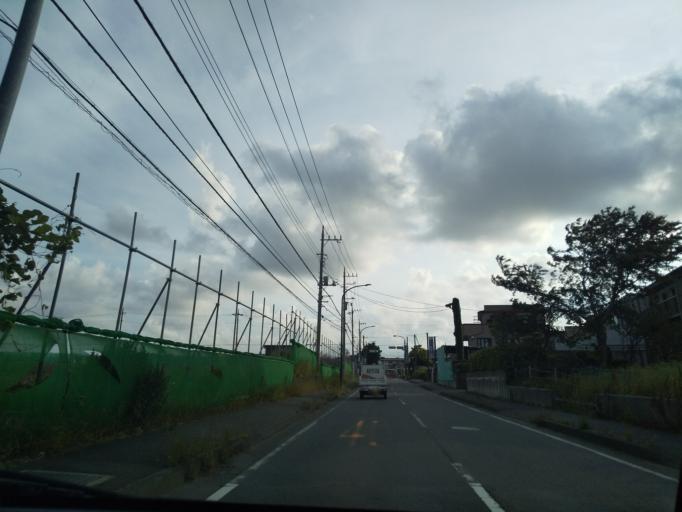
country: JP
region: Kanagawa
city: Zama
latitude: 35.5211
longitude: 139.3982
